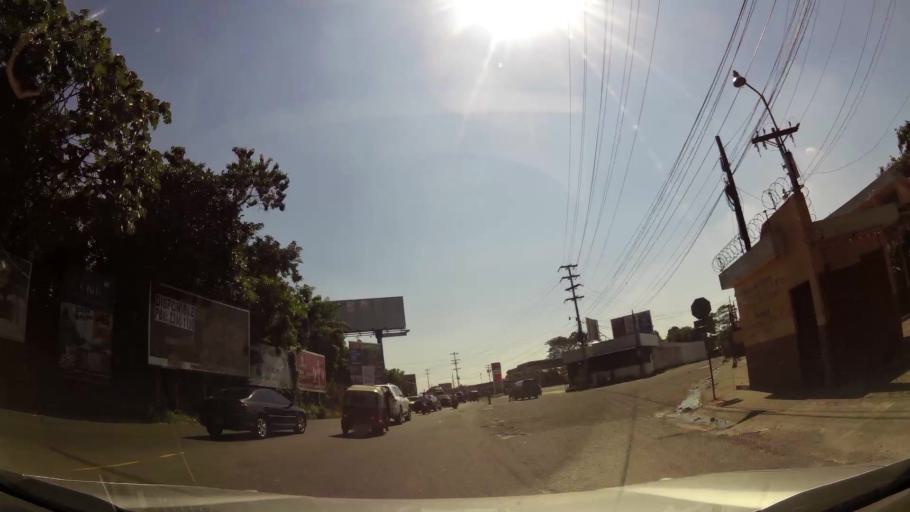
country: GT
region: Suchitepeque
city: Mazatenango
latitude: 14.5370
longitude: -91.4989
